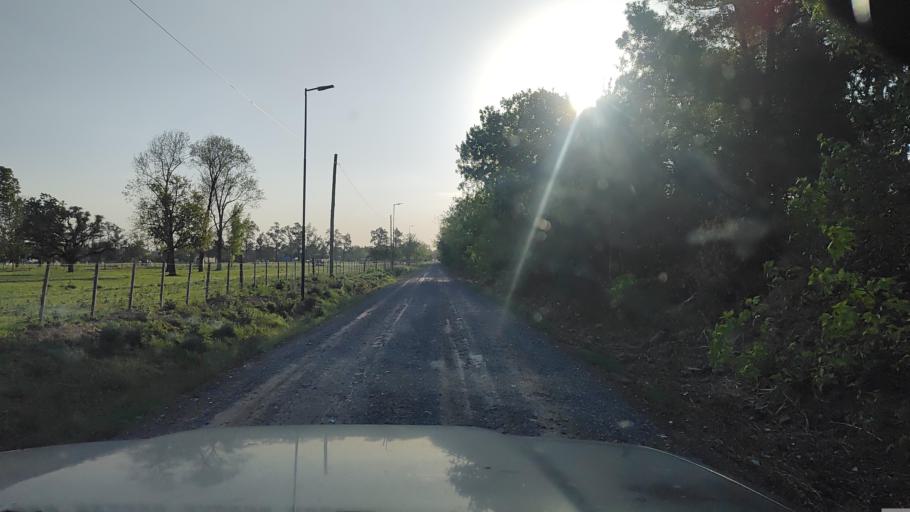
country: AR
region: Buenos Aires
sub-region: Partido de Lujan
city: Lujan
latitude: -34.5511
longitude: -59.1977
